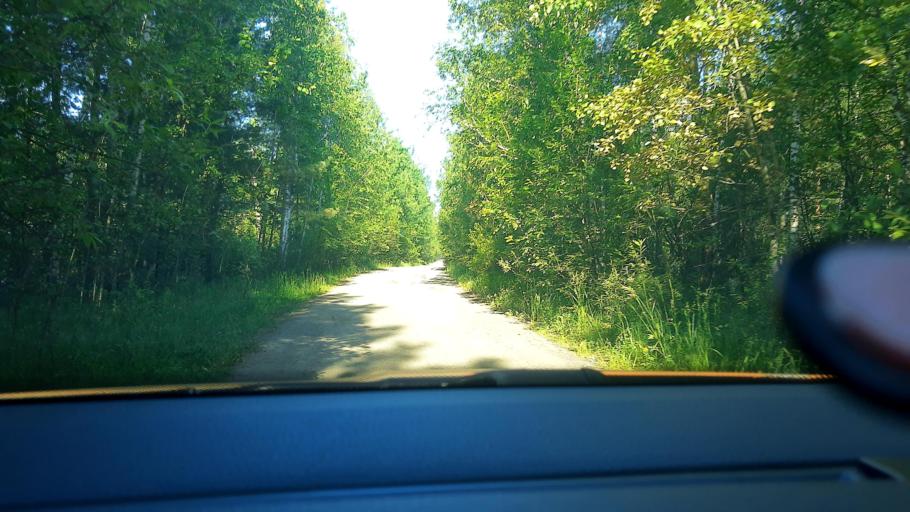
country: RU
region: Moskovskaya
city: Elektrogorsk
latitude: 55.8934
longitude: 38.7254
